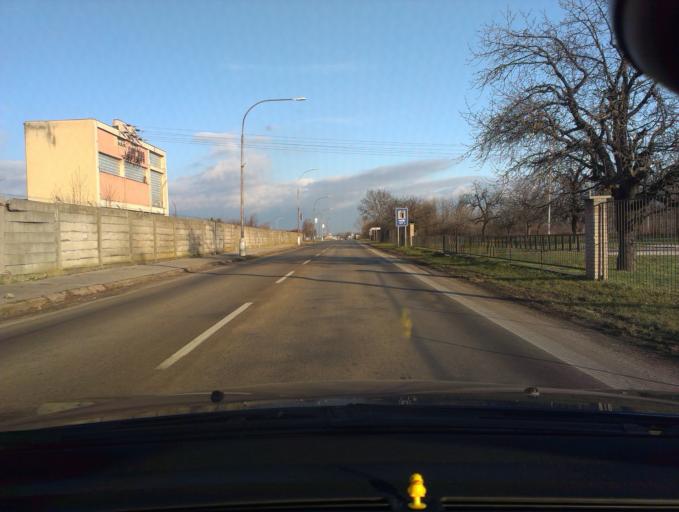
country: SK
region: Trnavsky
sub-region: Okres Trnava
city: Piestany
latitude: 48.6087
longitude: 17.8331
